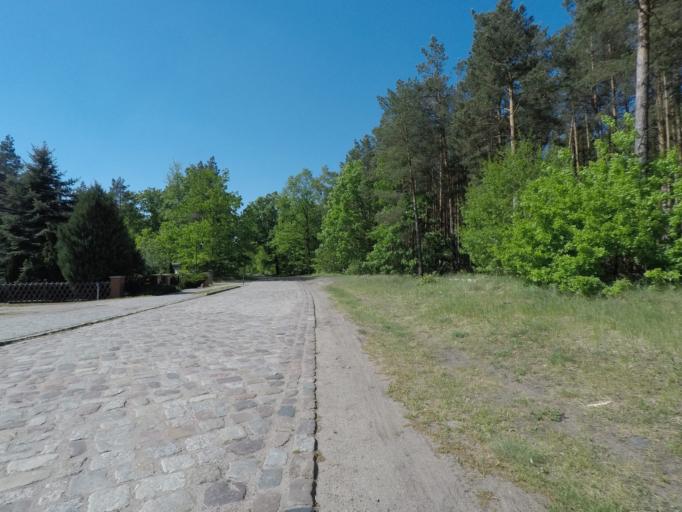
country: DE
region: Brandenburg
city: Eberswalde
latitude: 52.8129
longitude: 13.7729
